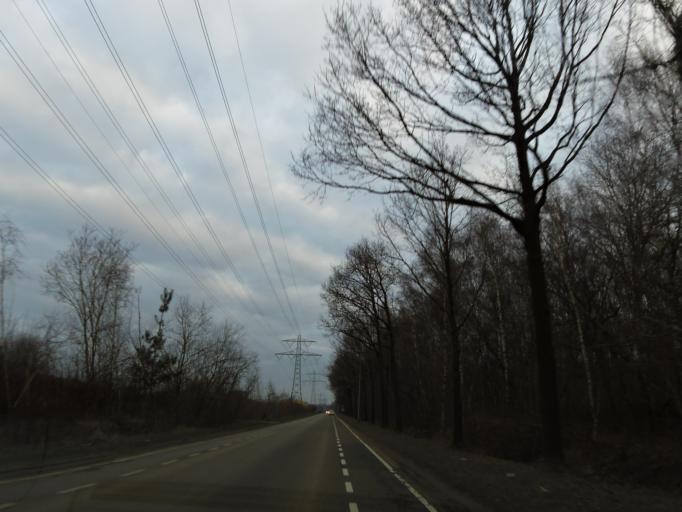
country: NL
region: Limburg
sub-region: Gemeente Onderbanken
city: Schinveld
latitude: 50.9428
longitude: 6.0161
